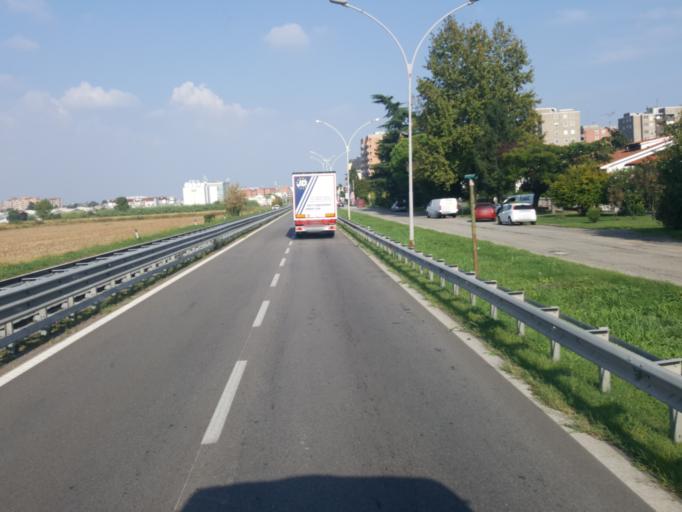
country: IT
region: Lombardy
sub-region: Citta metropolitana di Milano
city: Trezzano sul Naviglio
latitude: 45.4170
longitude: 9.0480
